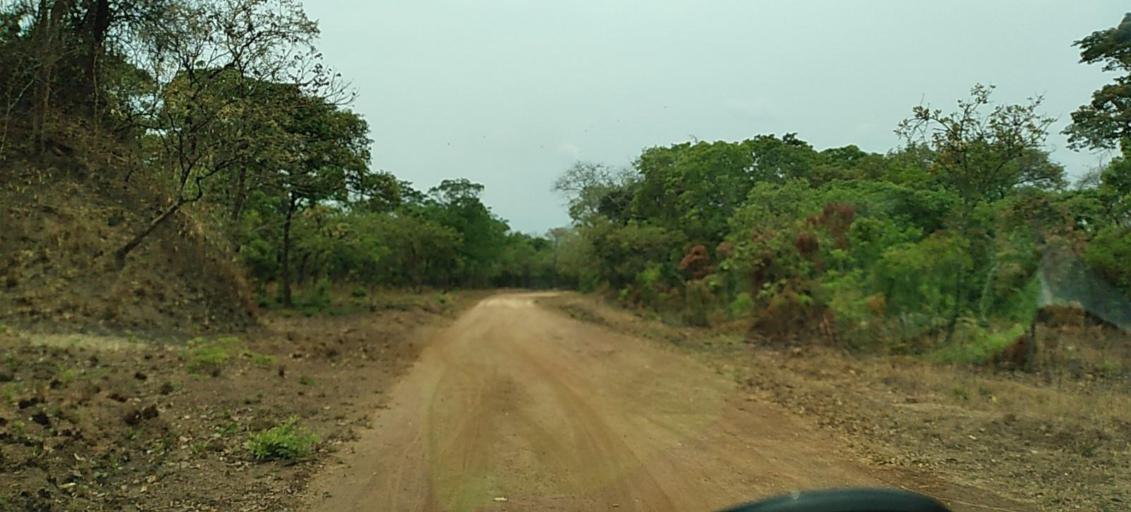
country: ZM
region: North-Western
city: Solwezi
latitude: -12.7830
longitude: 26.5195
